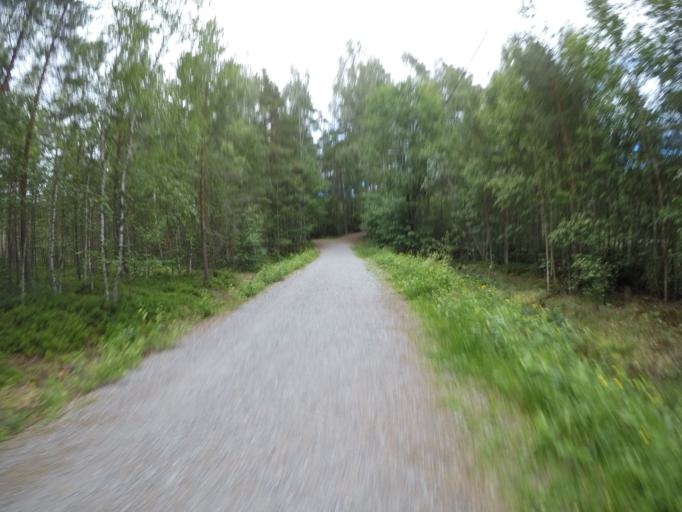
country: FI
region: Haeme
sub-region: Haemeenlinna
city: Haemeenlinna
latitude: 60.9961
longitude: 24.4141
